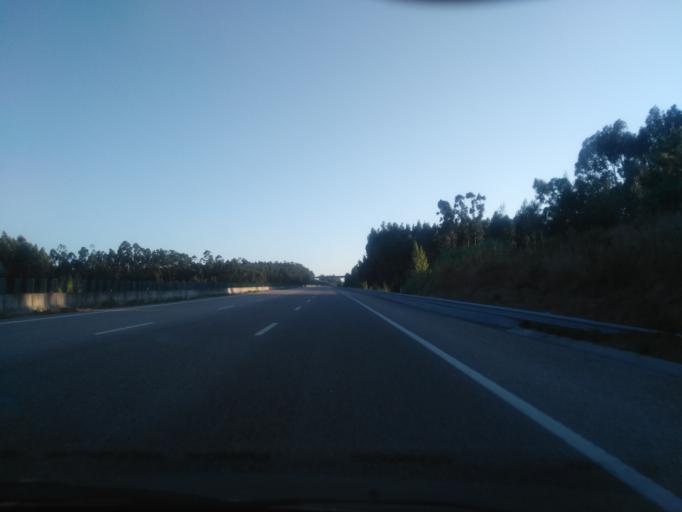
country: PT
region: Coimbra
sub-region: Figueira da Foz
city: Lavos
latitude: 40.0869
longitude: -8.7654
